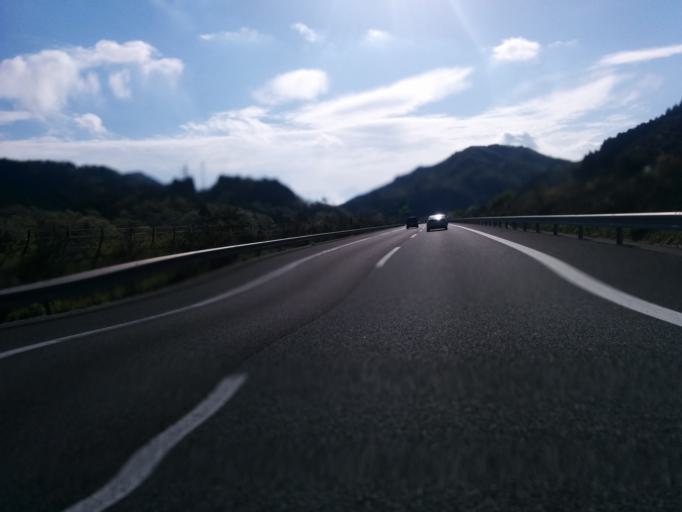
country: JP
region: Shiga Prefecture
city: Minakuchicho-matoba
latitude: 34.9232
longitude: 136.1001
